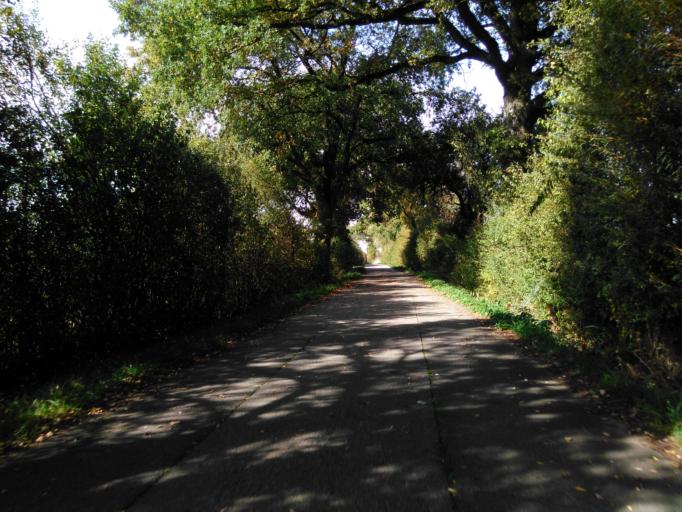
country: LU
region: Luxembourg
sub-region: Canton de Capellen
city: Bascharage
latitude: 49.5576
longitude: 5.9117
